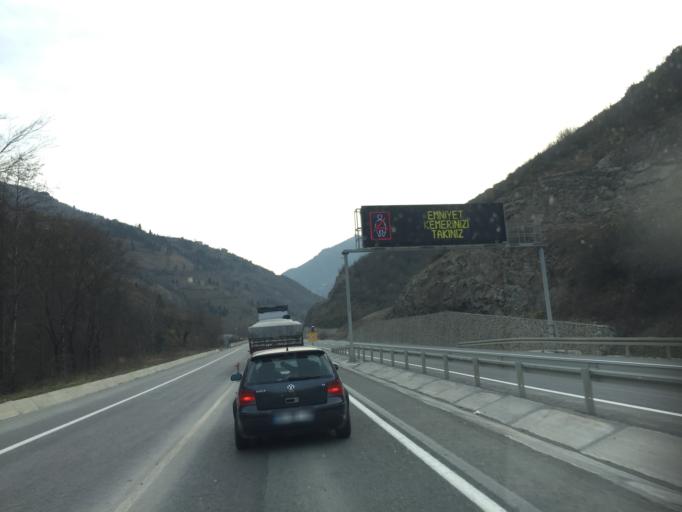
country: TR
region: Trabzon
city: Macka
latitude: 40.7927
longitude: 39.5818
